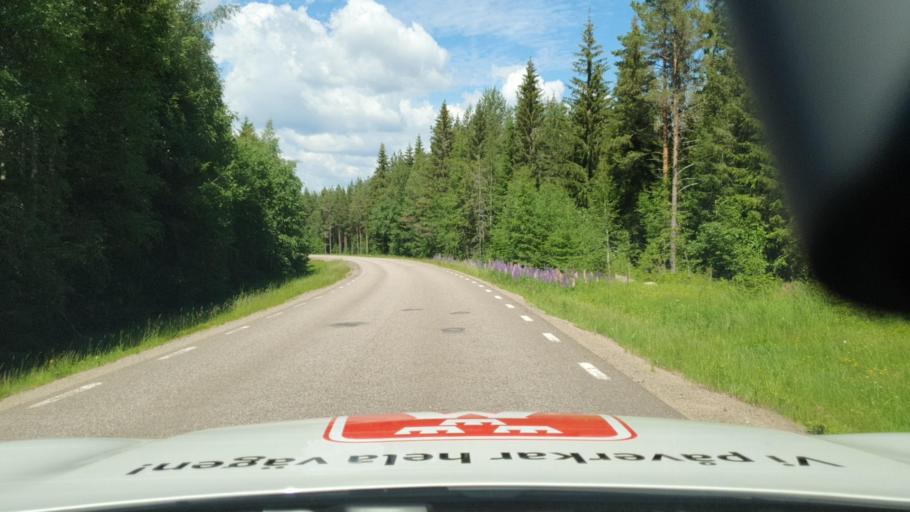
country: SE
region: Vaermland
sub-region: Torsby Kommun
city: Torsby
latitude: 60.4350
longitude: 12.9001
